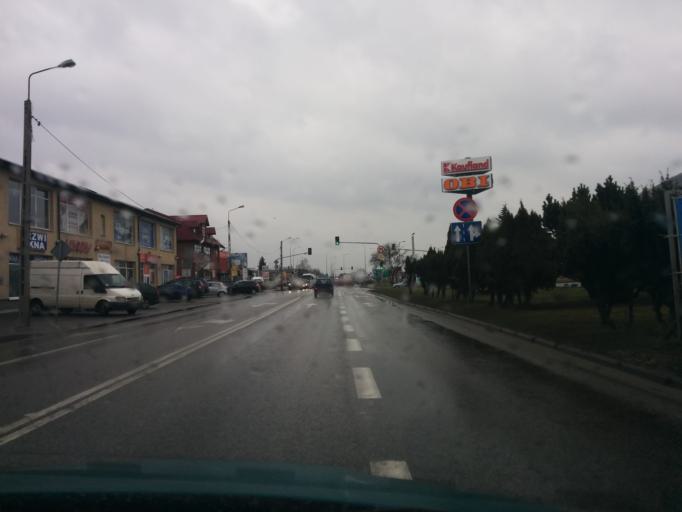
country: PL
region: Masovian Voivodeship
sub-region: Powiat legionowski
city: Jablonna
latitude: 52.3794
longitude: 20.9183
